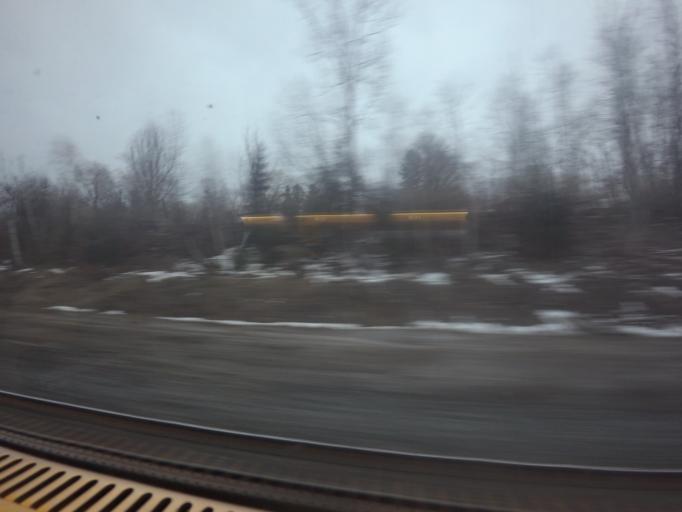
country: CA
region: Ontario
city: Scarborough
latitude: 43.7492
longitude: -79.2186
